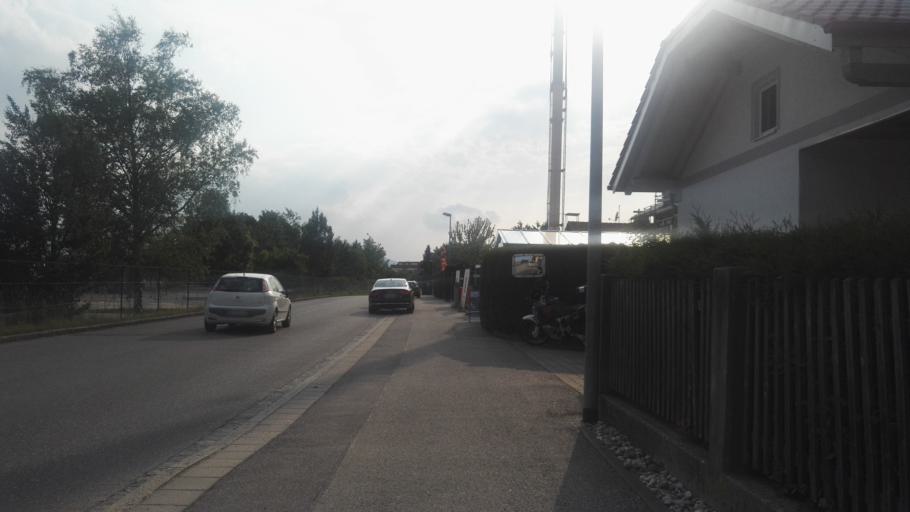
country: DE
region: Bavaria
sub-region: Upper Bavaria
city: Freilassing
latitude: 47.8389
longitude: 12.9663
